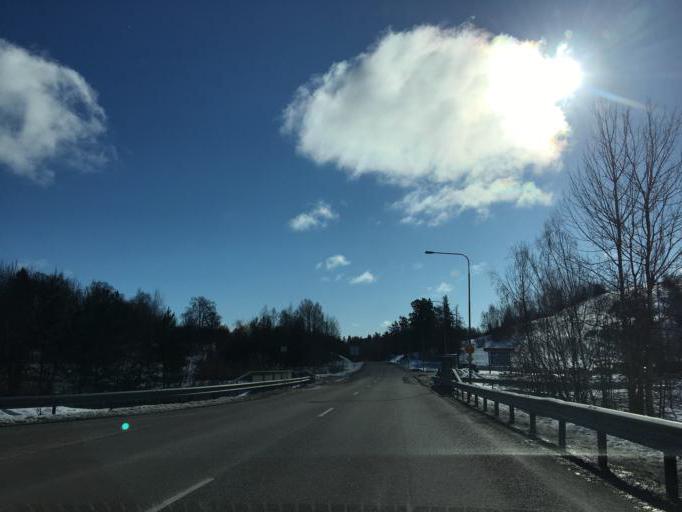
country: SE
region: Vaestmanland
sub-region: Vasteras
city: Vasteras
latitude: 59.6274
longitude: 16.4827
